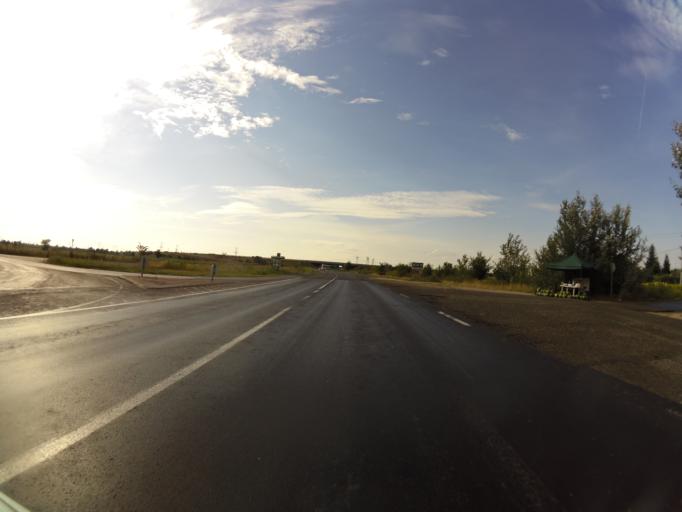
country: HU
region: Csongrad
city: Szatymaz
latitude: 46.2905
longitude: 20.0853
